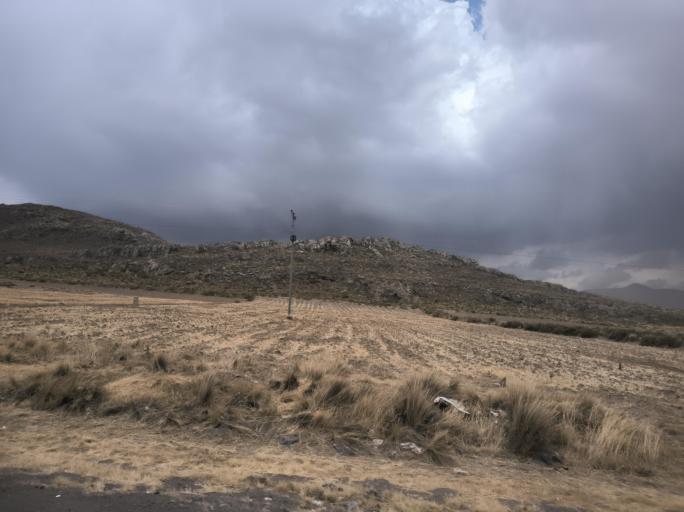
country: BO
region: Oruro
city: Challapata
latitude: -18.7670
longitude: -66.8582
